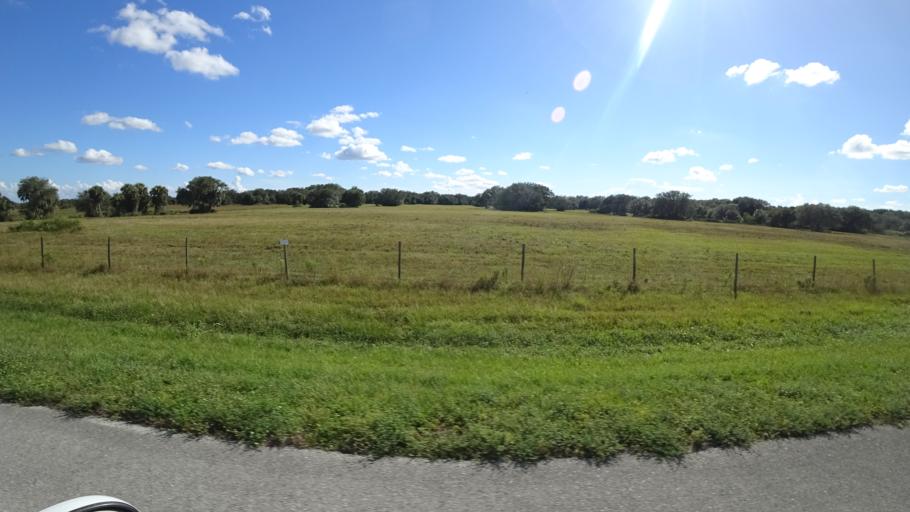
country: US
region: Florida
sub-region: Sarasota County
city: Warm Mineral Springs
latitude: 27.1935
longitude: -82.1738
